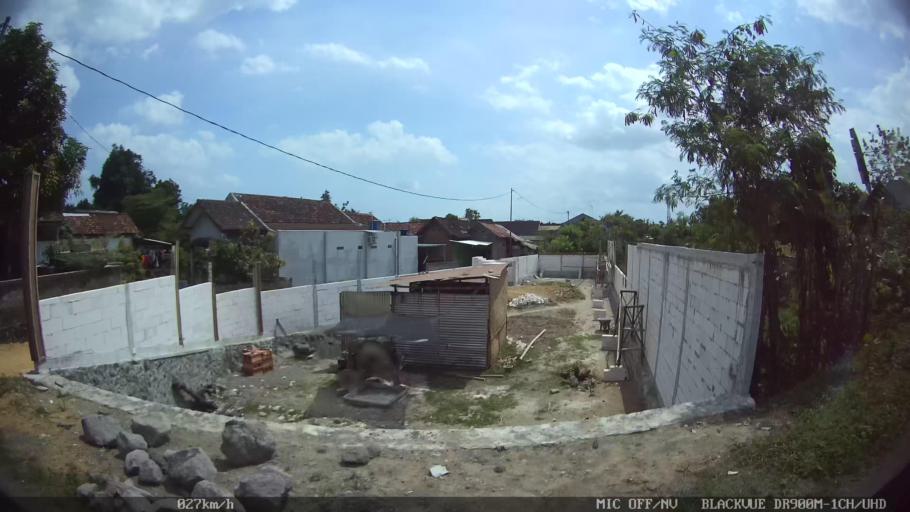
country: ID
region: Daerah Istimewa Yogyakarta
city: Kasihan
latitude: -7.8146
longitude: 110.3404
